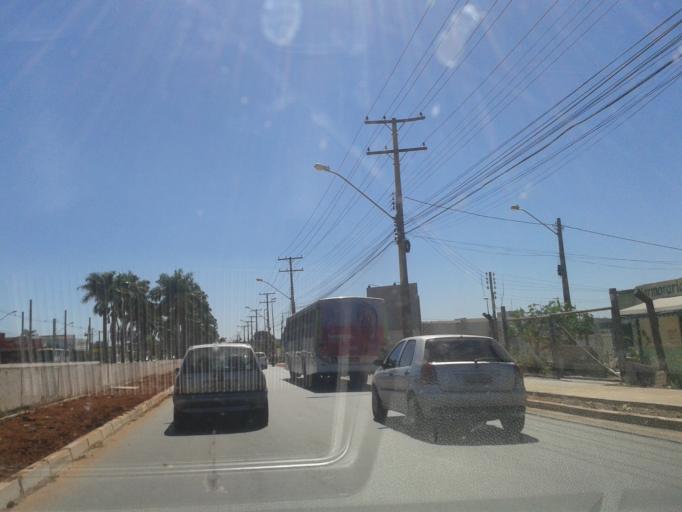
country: BR
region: Goias
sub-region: Goiania
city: Goiania
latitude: -16.6509
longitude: -49.2640
